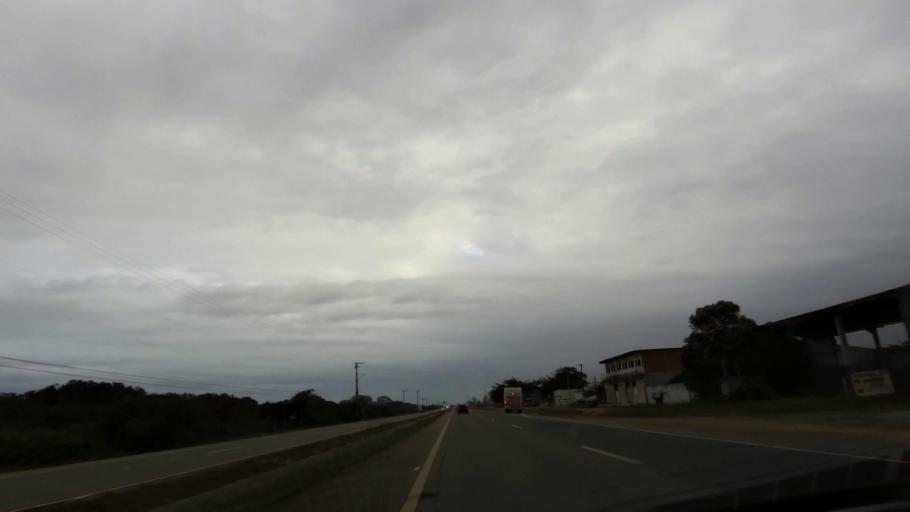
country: BR
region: Espirito Santo
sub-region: Guarapari
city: Guarapari
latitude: -20.5528
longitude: -40.4010
